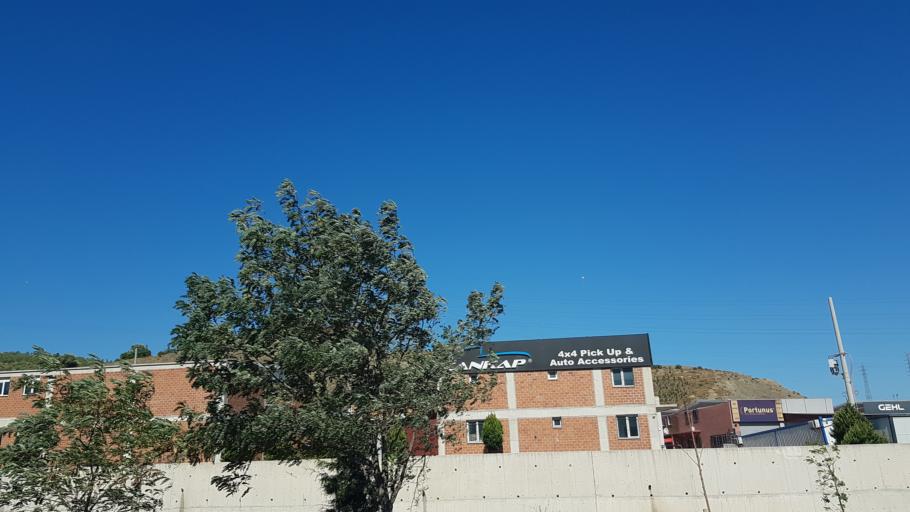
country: TR
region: Izmir
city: Bornova
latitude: 38.4119
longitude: 27.2376
